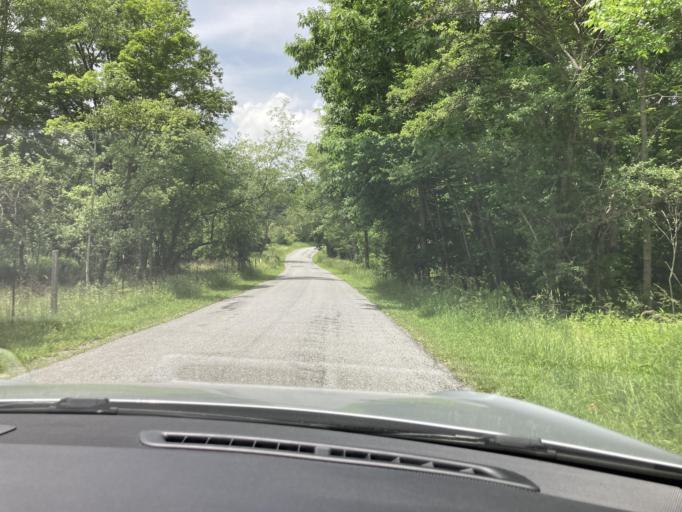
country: US
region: Pennsylvania
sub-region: Somerset County
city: Boswell
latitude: 40.1698
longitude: -79.0926
